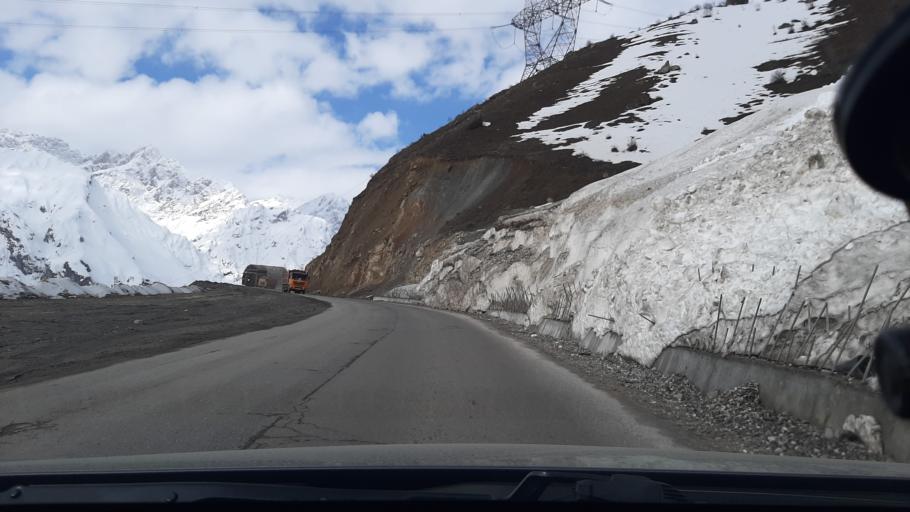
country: TJ
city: Tagob
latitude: 39.0630
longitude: 68.7149
